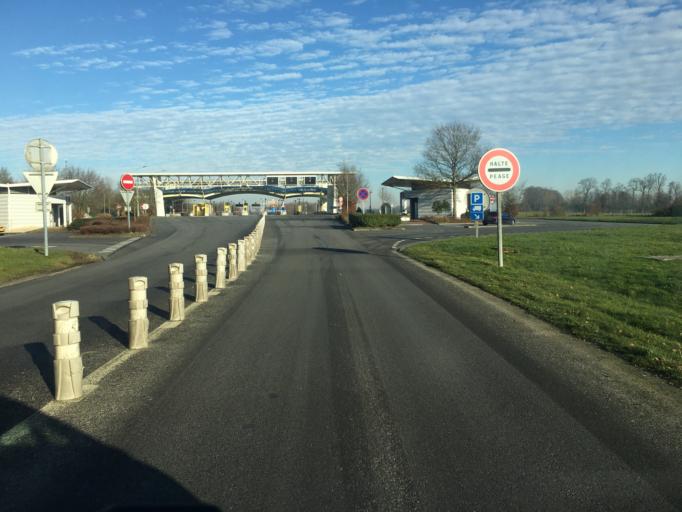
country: FR
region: Haute-Normandie
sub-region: Departement de la Seine-Maritime
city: Yerville
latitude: 49.6463
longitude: 0.8417
